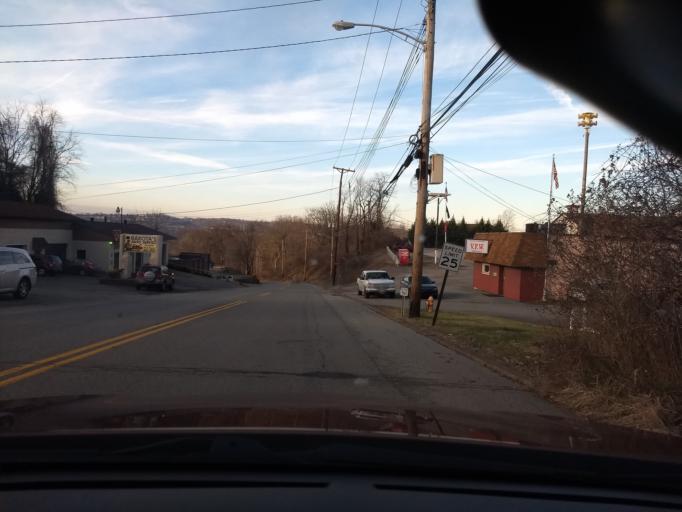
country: US
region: Pennsylvania
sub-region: Allegheny County
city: Whitaker
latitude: 40.4039
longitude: -79.8905
